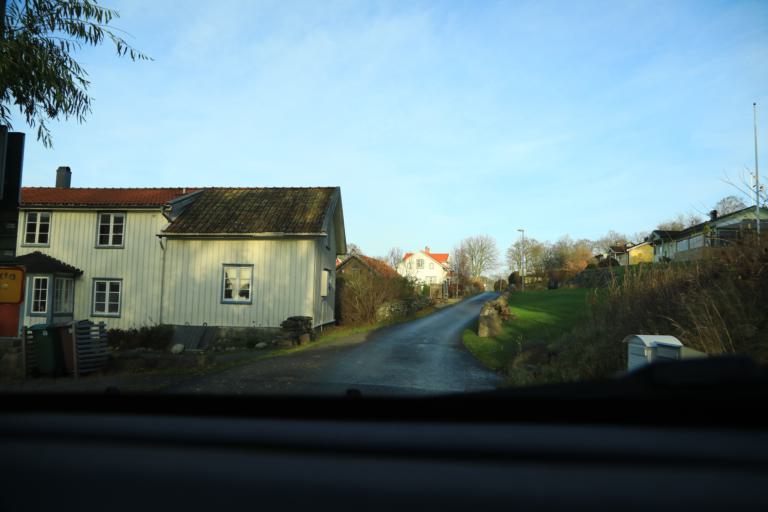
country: SE
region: Halland
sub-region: Varbergs Kommun
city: Varberg
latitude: 57.1903
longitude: 12.2143
